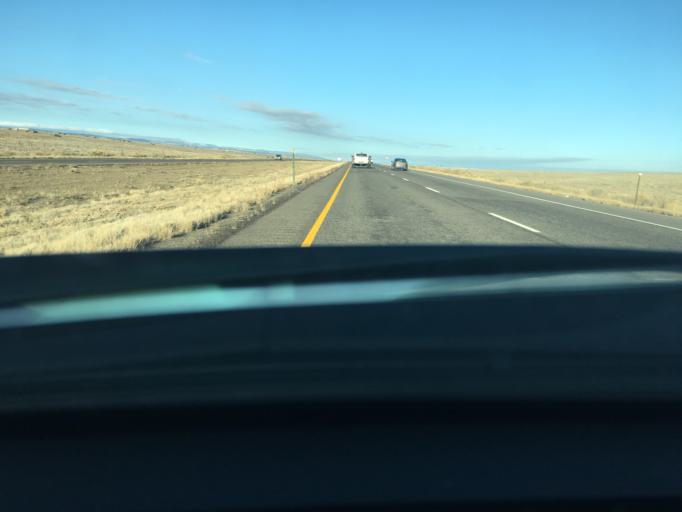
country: US
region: Colorado
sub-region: Delta County
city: Delta
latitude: 38.7801
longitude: -108.2387
